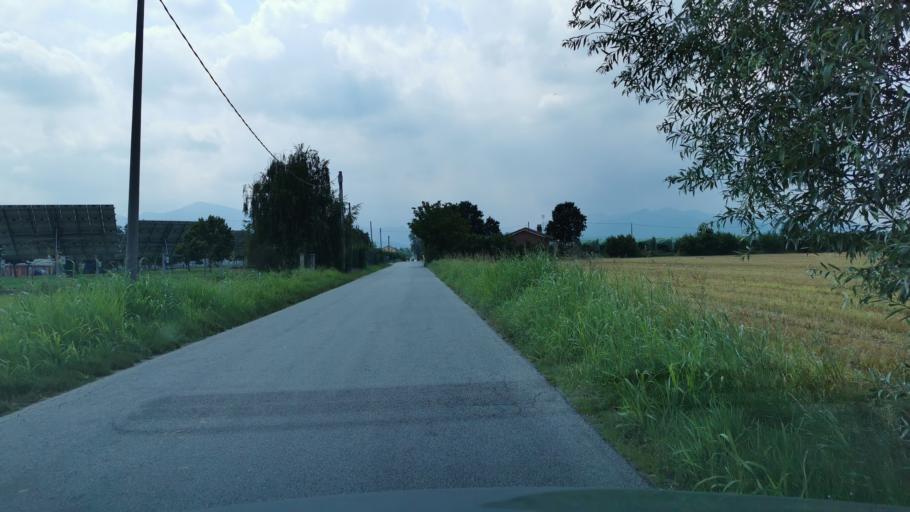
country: IT
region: Piedmont
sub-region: Provincia di Cuneo
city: San Rocco
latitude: 44.4285
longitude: 7.4749
